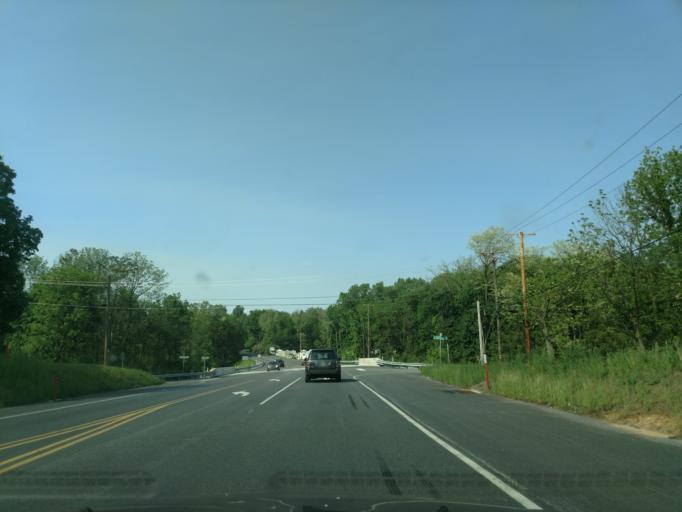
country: US
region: Pennsylvania
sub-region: Lebanon County
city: Cornwall
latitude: 40.2886
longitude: -76.4270
